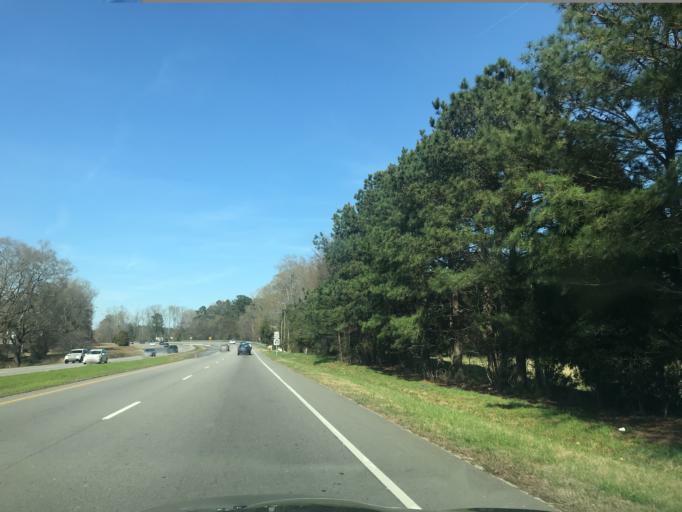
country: US
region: North Carolina
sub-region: Wake County
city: Garner
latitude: 35.6704
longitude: -78.6928
